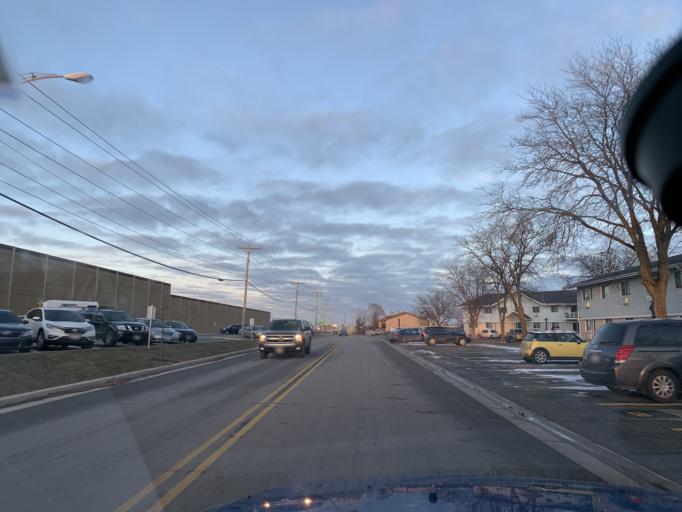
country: US
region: Wisconsin
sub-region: Dane County
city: Shorewood Hills
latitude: 43.0289
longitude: -89.4627
